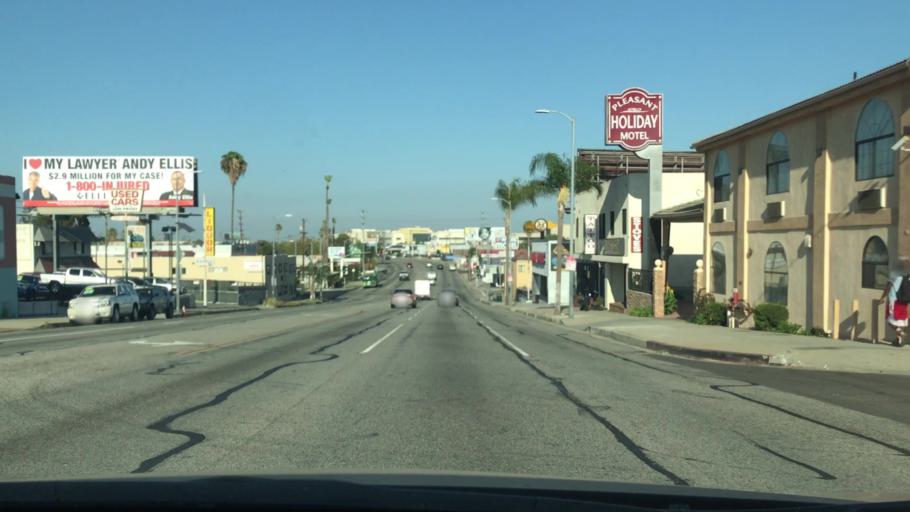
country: US
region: California
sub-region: Los Angeles County
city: Lomita
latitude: 33.7894
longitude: -118.3027
